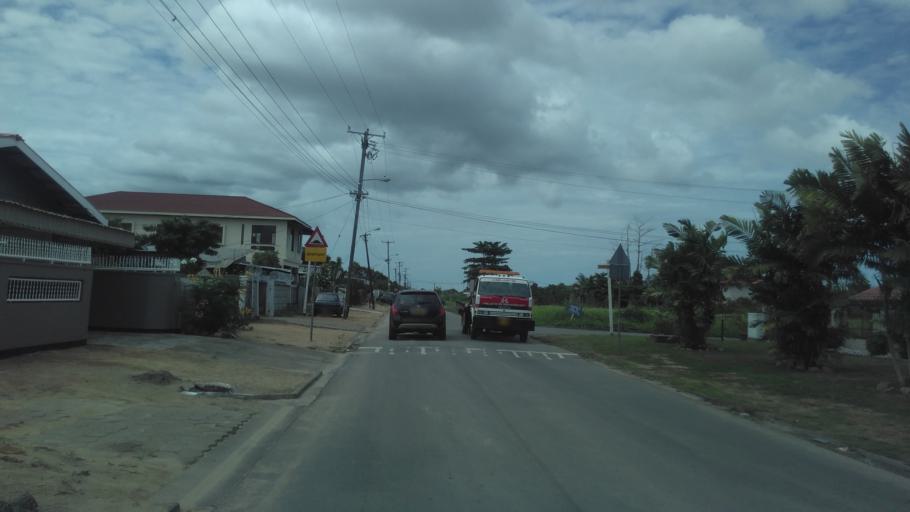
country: SR
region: Paramaribo
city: Paramaribo
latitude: 5.8456
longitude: -55.1215
